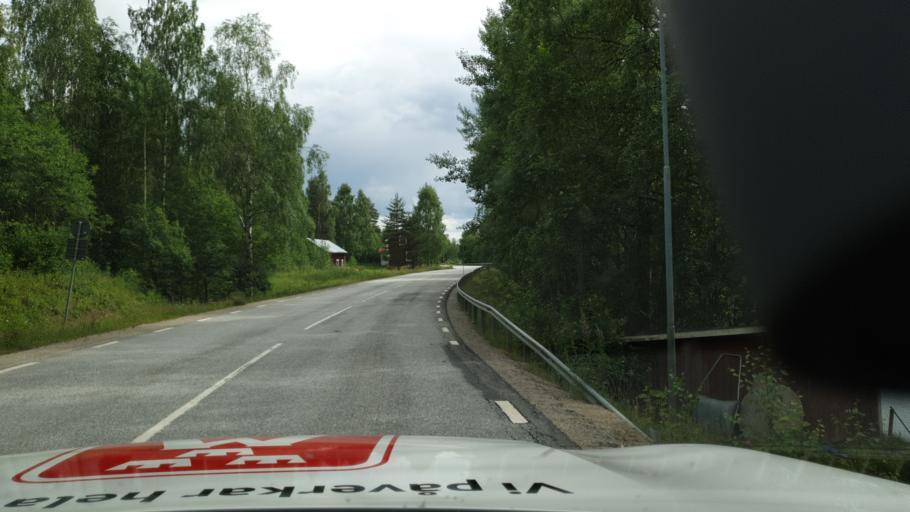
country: SE
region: Vaesterbotten
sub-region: Vindelns Kommun
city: Vindeln
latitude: 64.1523
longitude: 19.5114
